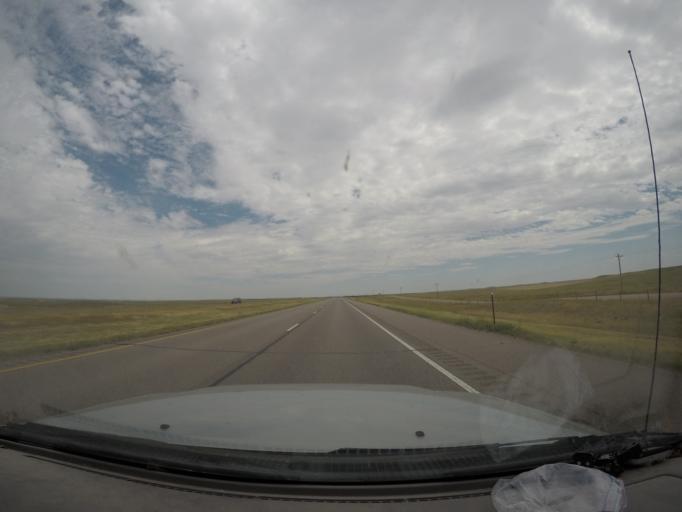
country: US
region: Nebraska
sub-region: Kimball County
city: Kimball
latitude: 41.1917
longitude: -103.7946
